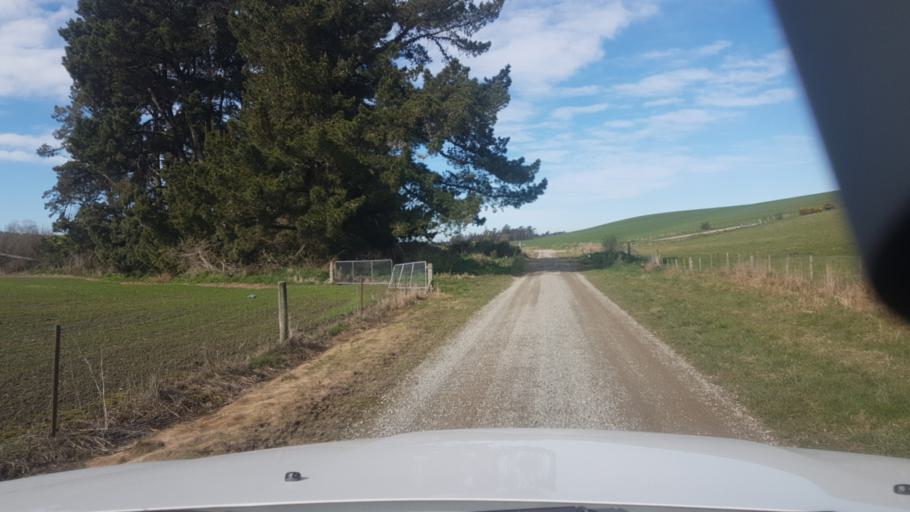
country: NZ
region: Canterbury
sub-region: Timaru District
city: Pleasant Point
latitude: -44.2014
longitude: 171.1851
